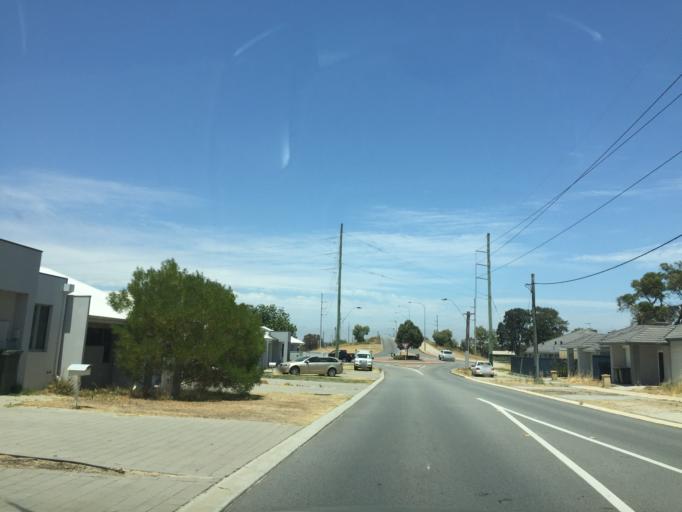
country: AU
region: Western Australia
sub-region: Canning
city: Cannington
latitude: -32.0140
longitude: 115.9489
